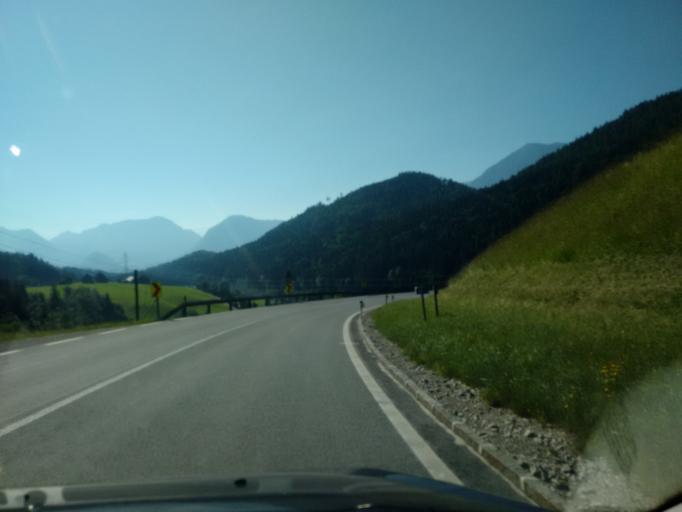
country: AT
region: Styria
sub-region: Politischer Bezirk Liezen
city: Altaussee
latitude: 47.6294
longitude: 13.7309
